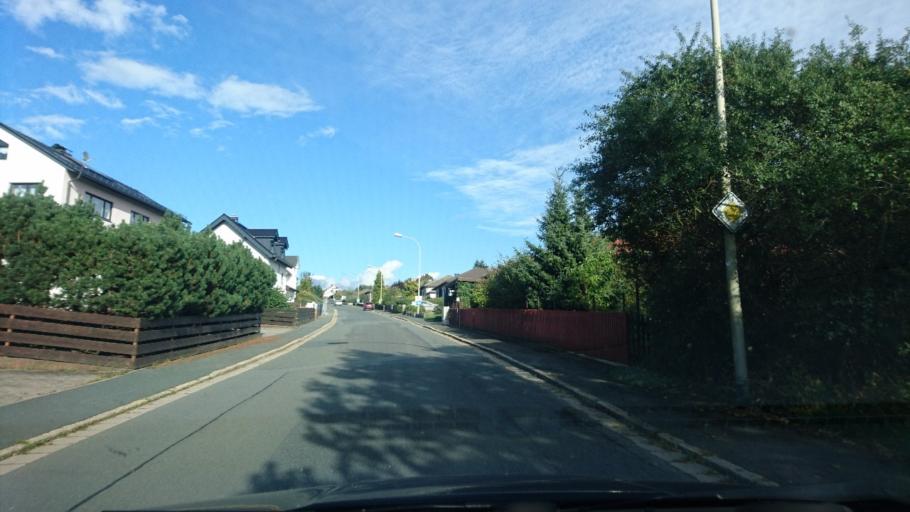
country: DE
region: Bavaria
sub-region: Upper Franconia
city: Naila
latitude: 50.3380
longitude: 11.7185
